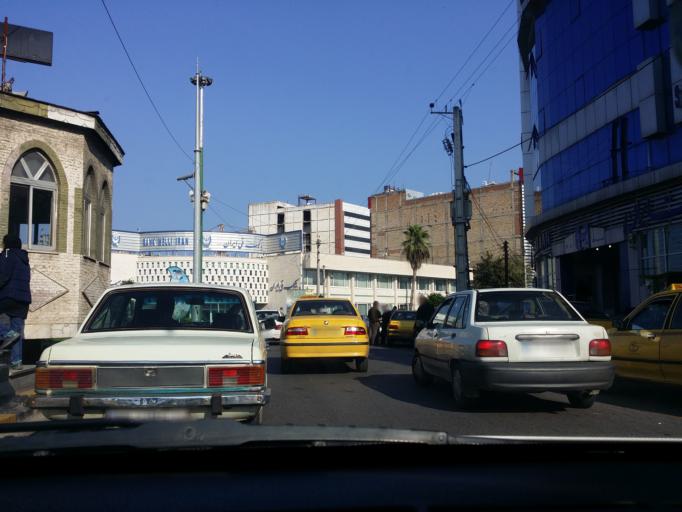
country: IR
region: Mazandaran
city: Chalus
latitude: 36.6543
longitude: 51.4213
